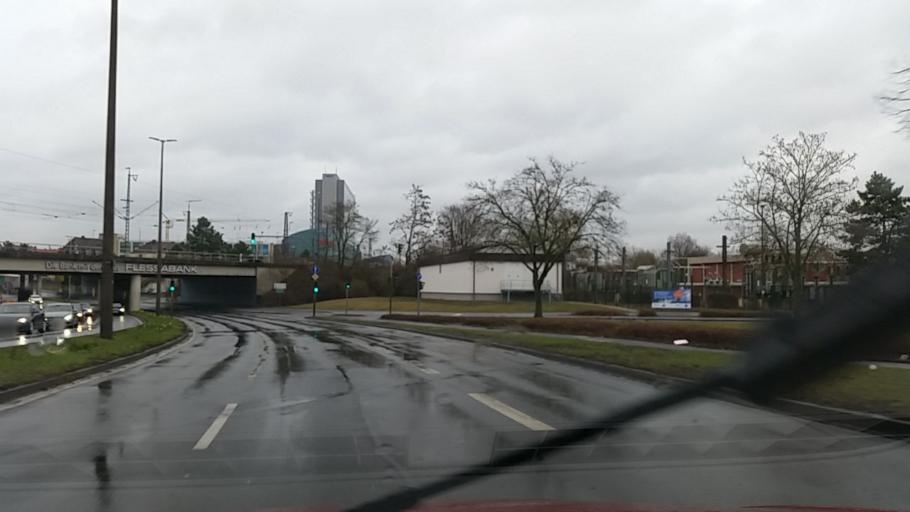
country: DE
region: Bavaria
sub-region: Regierungsbezirk Unterfranken
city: Schweinfurt
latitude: 50.0364
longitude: 10.2207
